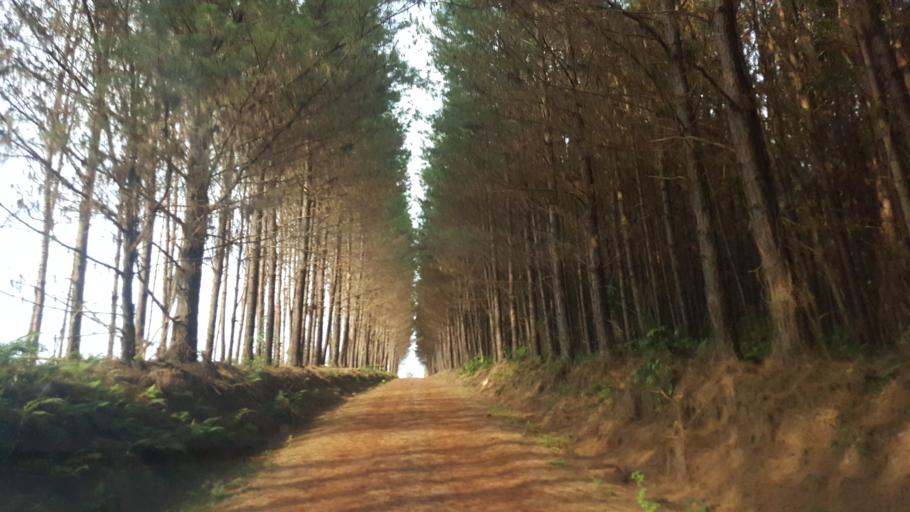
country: AR
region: Misiones
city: Capiovi
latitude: -26.9103
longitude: -55.1168
